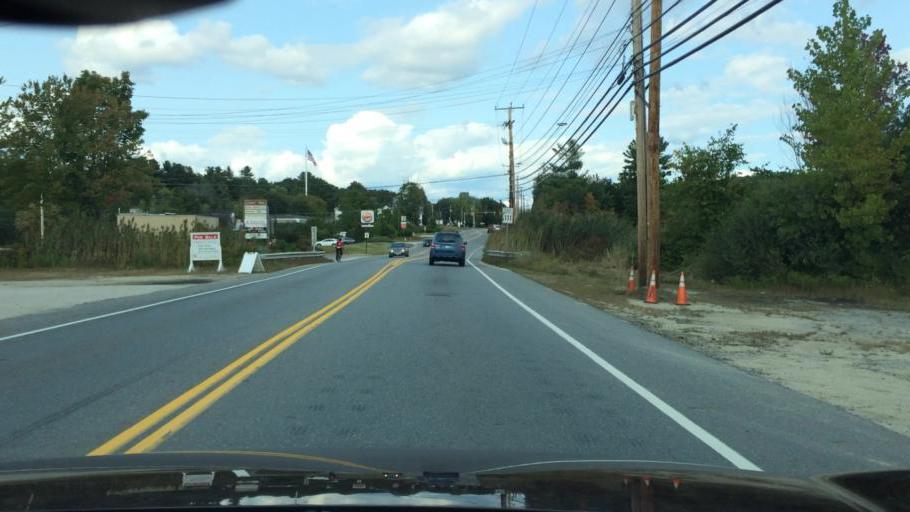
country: US
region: New Hampshire
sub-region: Hillsborough County
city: Hudson
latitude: 42.7695
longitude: -71.4116
